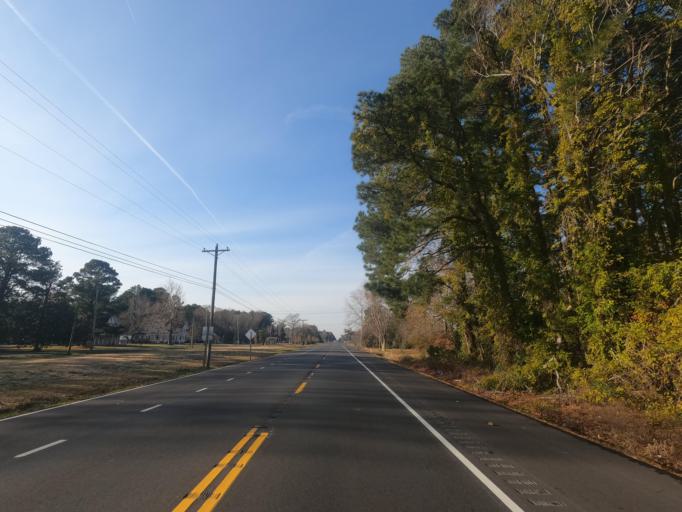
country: US
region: Maryland
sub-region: Somerset County
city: Crisfield
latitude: 38.0372
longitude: -75.7749
